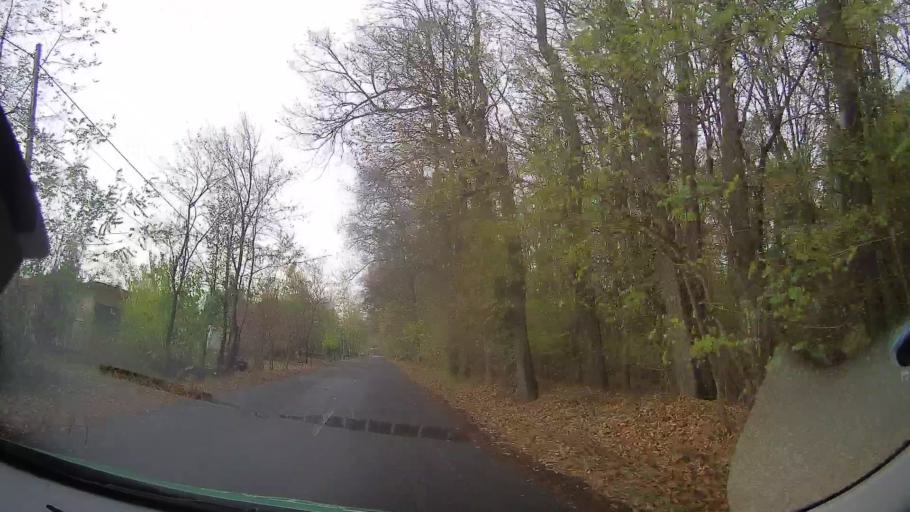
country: RO
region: Ilfov
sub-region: Comuna Snagov
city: Snagov
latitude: 44.7155
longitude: 26.1921
